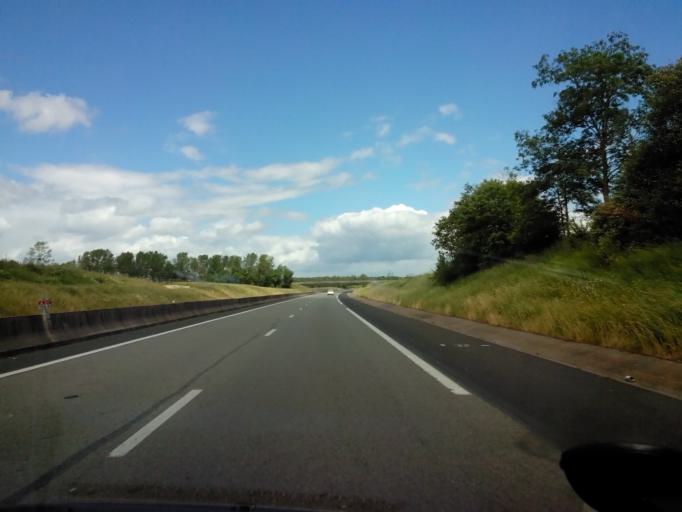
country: FR
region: Lorraine
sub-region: Departement des Vosges
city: Lamarche
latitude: 48.1233
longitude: 5.6646
